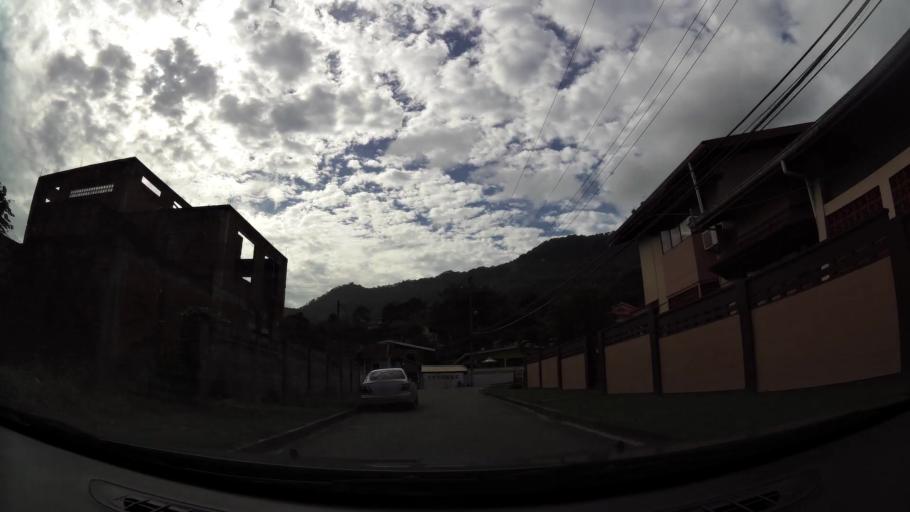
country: TT
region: Diego Martin
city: Petit Valley
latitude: 10.7133
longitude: -61.4798
